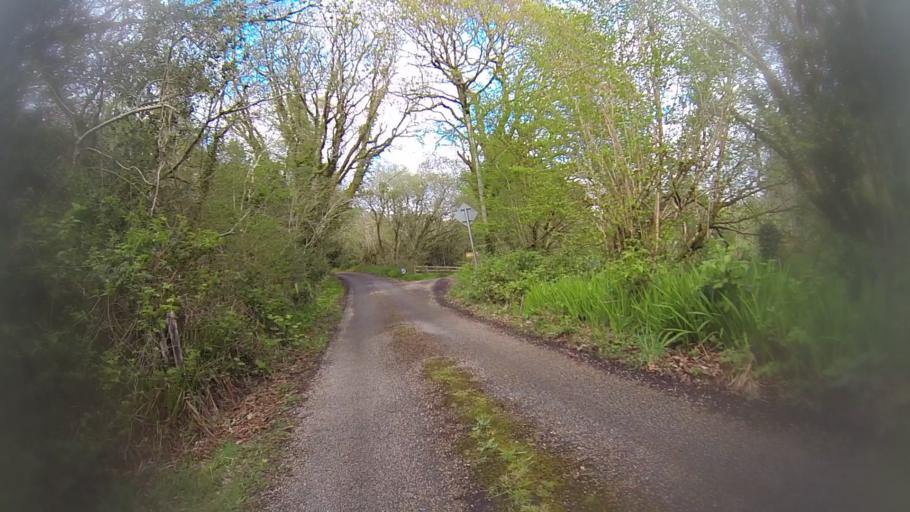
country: IE
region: Munster
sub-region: Ciarrai
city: Kenmare
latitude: 51.8623
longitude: -9.7109
